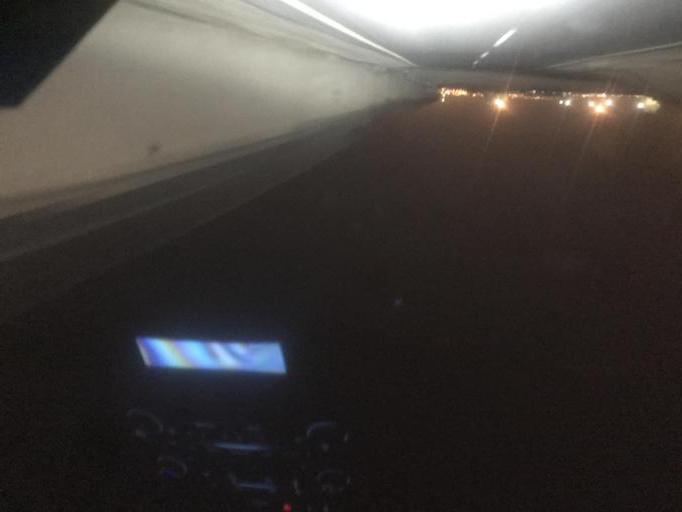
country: SA
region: Ar Riyad
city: Riyadh
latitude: 24.7635
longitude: 46.5869
